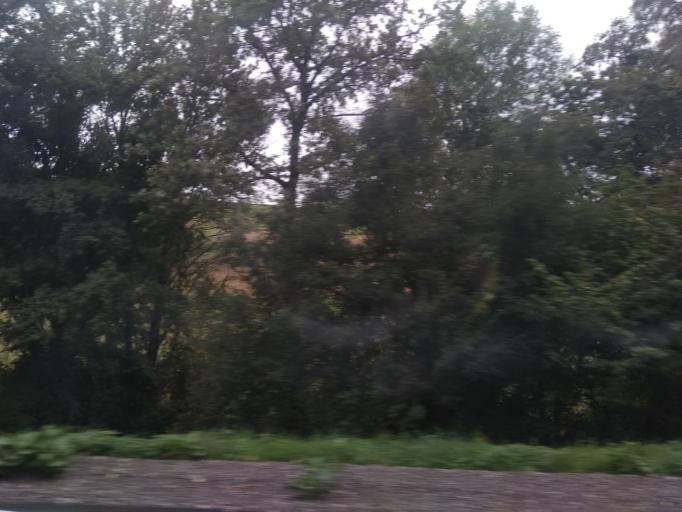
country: DE
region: Baden-Wuerttemberg
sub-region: Karlsruhe Region
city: Billigheim
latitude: 49.3540
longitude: 9.2679
